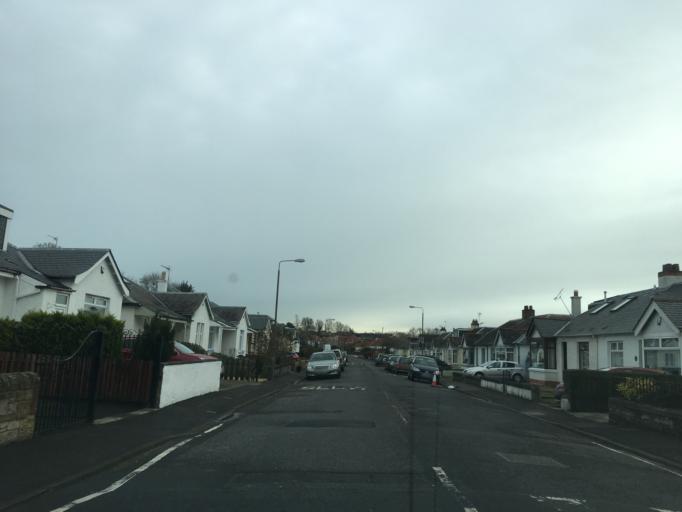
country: GB
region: Scotland
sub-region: Edinburgh
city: Colinton
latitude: 55.9403
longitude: -3.2738
